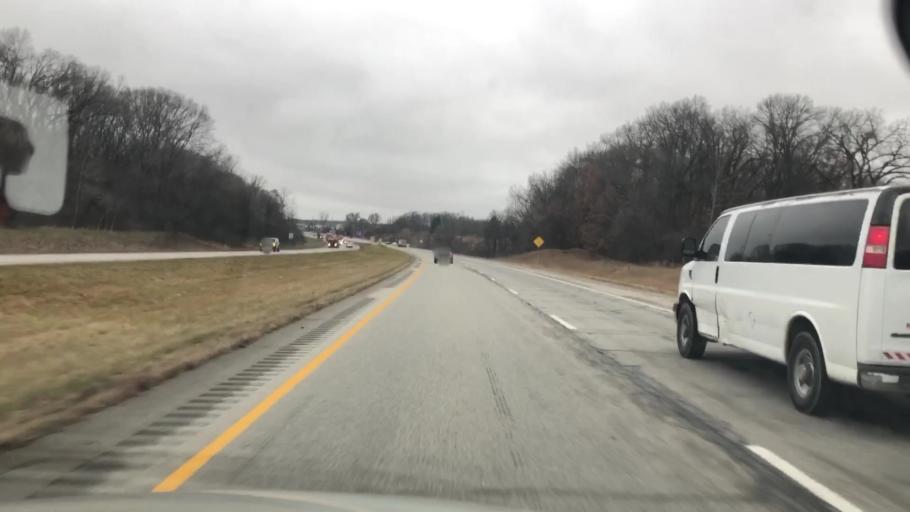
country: US
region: Indiana
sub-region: Kosciusko County
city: Warsaw
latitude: 41.2578
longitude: -85.8327
